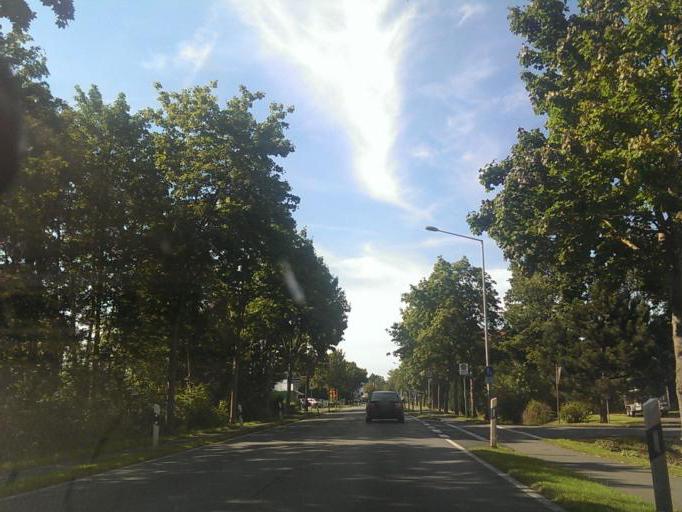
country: DE
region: North Rhine-Westphalia
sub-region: Regierungsbezirk Detmold
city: Hovelhof
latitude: 51.8167
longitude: 8.6620
